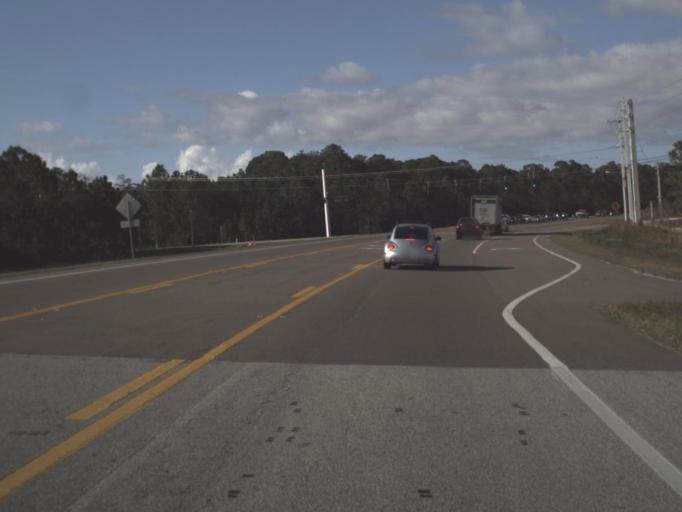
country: US
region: Florida
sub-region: Volusia County
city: Port Orange
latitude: 29.1156
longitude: -81.0465
